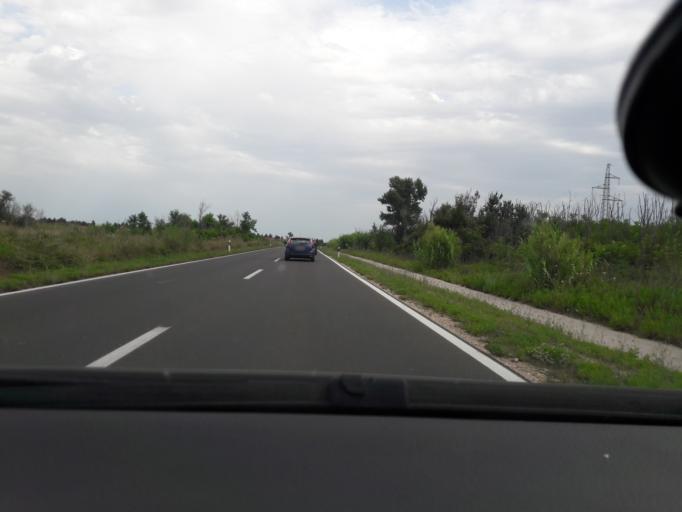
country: HR
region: Zadarska
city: Privlaka
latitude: 44.2602
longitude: 15.1495
